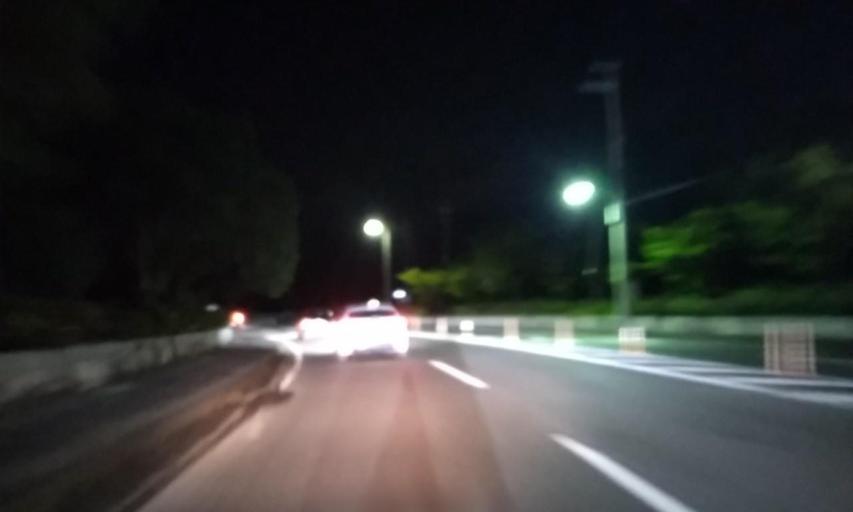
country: JP
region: Kyoto
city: Maizuru
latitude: 35.4789
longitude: 135.3900
